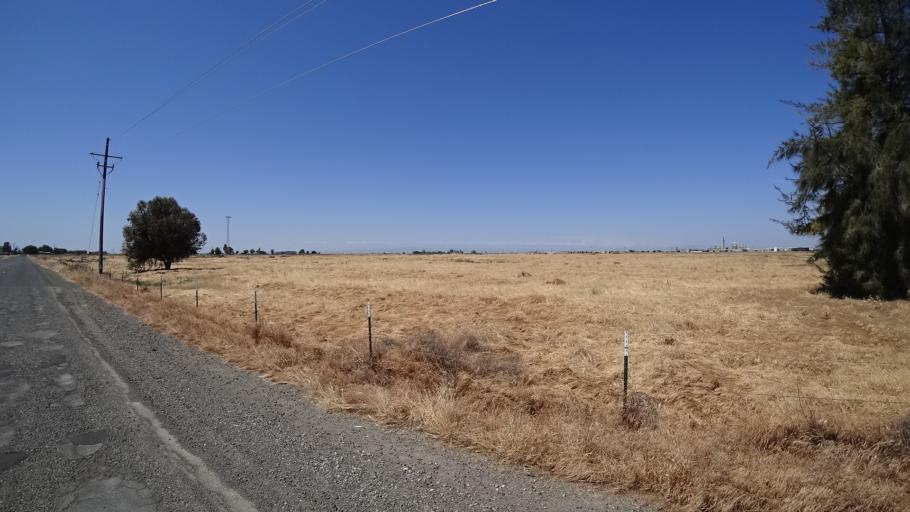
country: US
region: California
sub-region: Kings County
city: Lemoore
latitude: 36.2771
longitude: -119.7900
